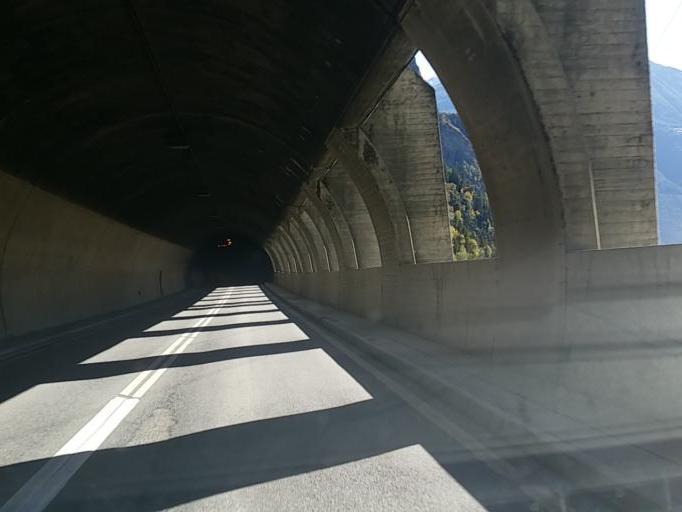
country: CH
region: Valais
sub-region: Leuk District
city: Gampel
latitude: 46.3423
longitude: 7.7545
